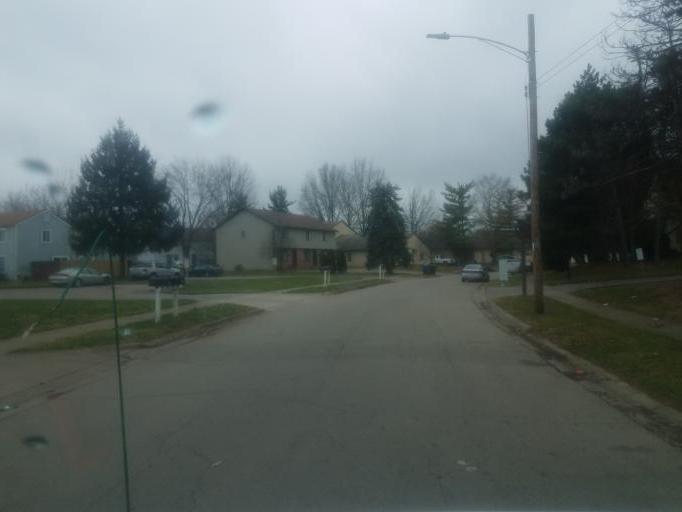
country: US
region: Ohio
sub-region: Franklin County
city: Minerva Park
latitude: 40.0923
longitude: -82.9526
